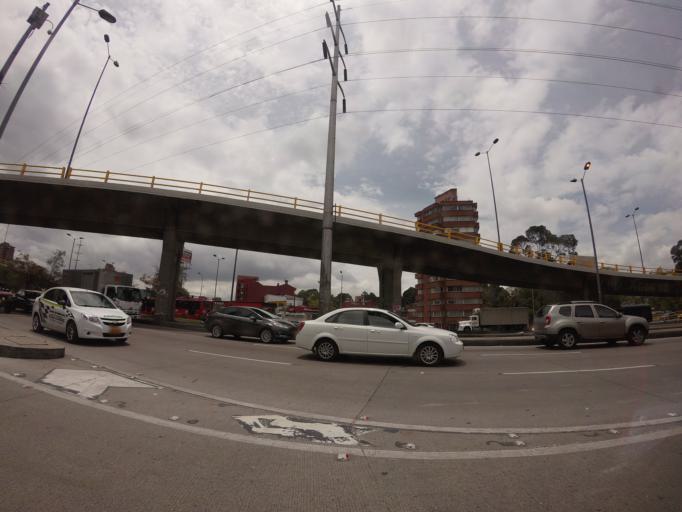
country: CO
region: Bogota D.C.
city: Bogota
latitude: 4.6331
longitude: -74.0795
